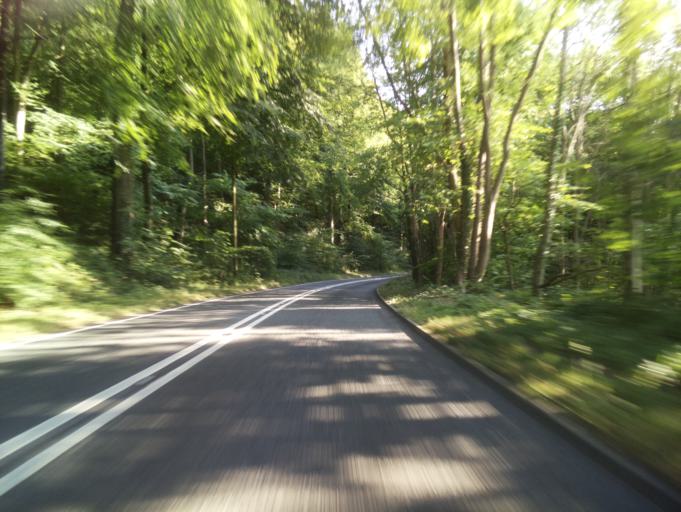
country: GB
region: England
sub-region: Gloucestershire
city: Painswick
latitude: 51.8194
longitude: -2.1686
